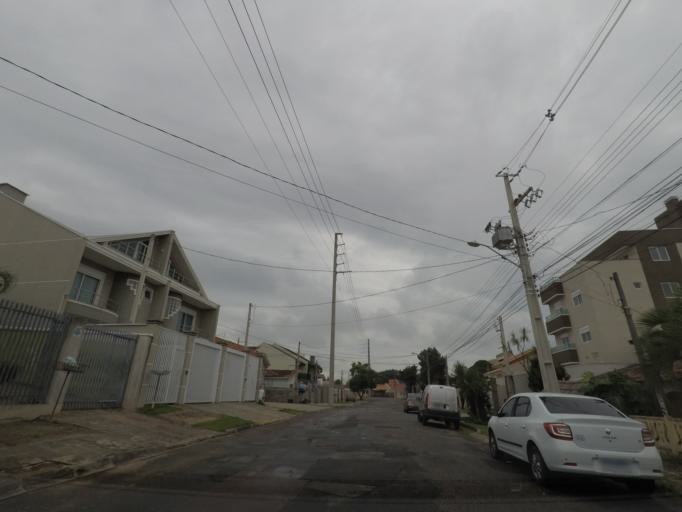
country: BR
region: Parana
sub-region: Curitiba
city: Curitiba
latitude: -25.4718
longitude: -49.3100
